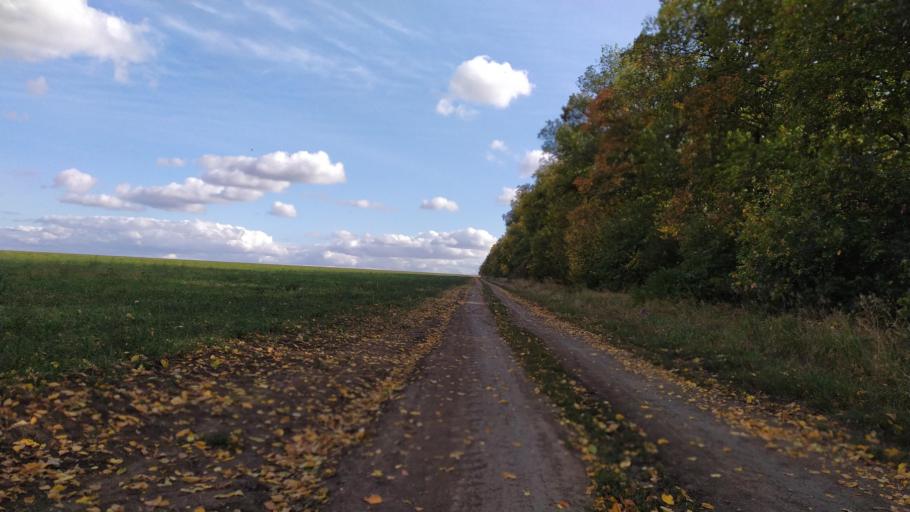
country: RU
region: Kursk
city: Kursk
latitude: 51.6216
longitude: 36.1616
